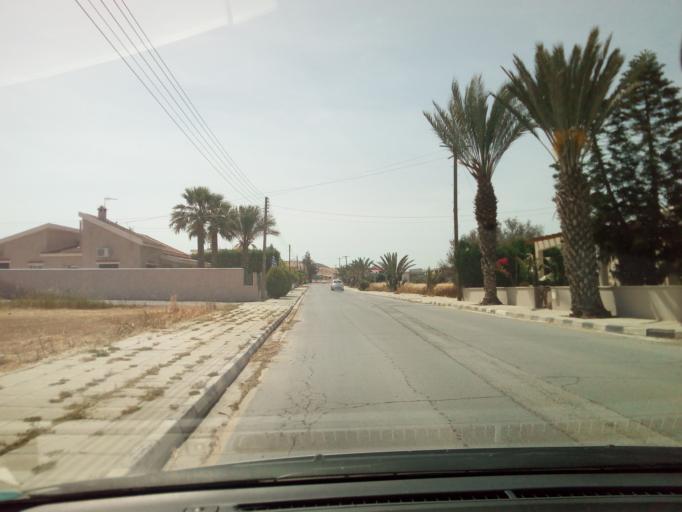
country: CY
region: Larnaka
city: Athienou
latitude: 35.0568
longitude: 33.5342
